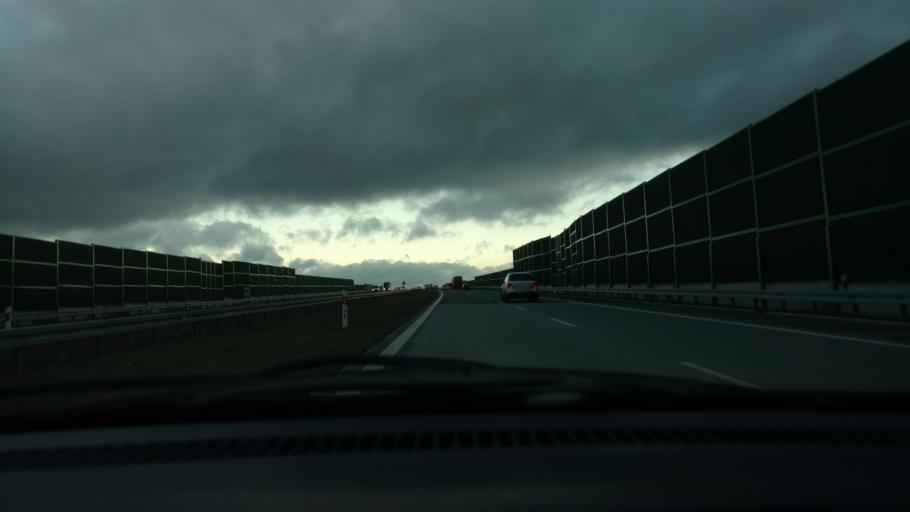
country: PL
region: Lodz Voivodeship
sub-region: Powiat lodzki wschodni
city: Andrespol
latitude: 51.7236
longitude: 19.6074
